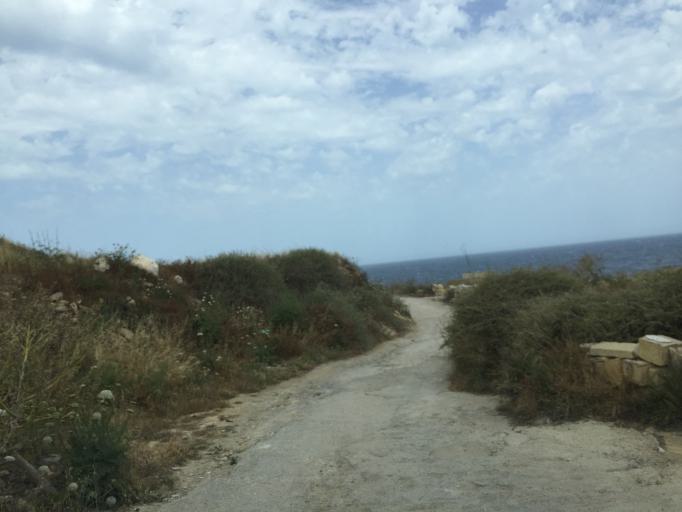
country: MT
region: Iz-Zebbug
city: Zebbug
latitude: 36.0791
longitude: 14.2313
